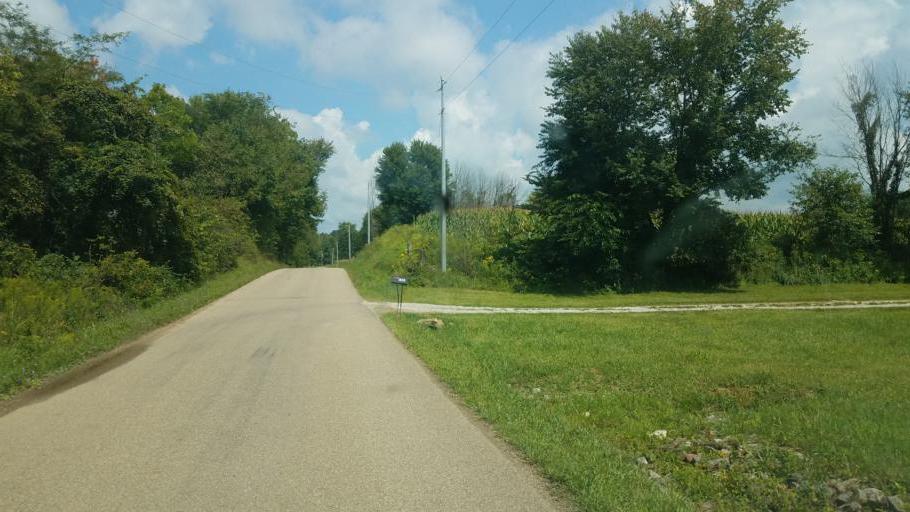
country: US
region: Ohio
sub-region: Licking County
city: Utica
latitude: 40.2606
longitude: -82.4358
